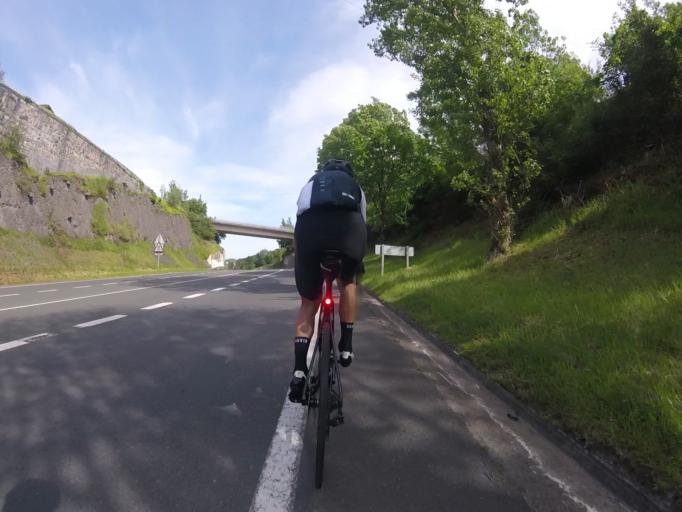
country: ES
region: Basque Country
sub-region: Provincia de Guipuzcoa
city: Cestona
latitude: 43.2559
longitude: -2.2676
